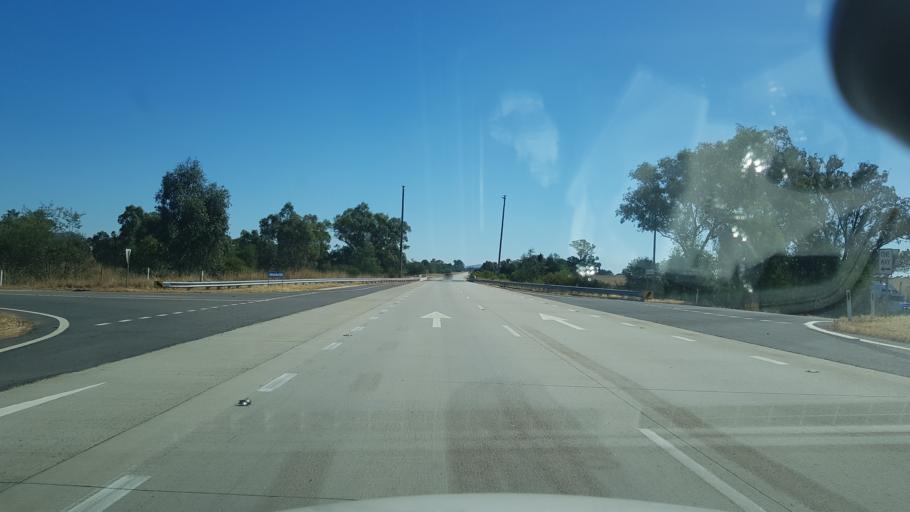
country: AU
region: New South Wales
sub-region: Greater Hume Shire
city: Jindera
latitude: -35.9253
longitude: 147.0336
